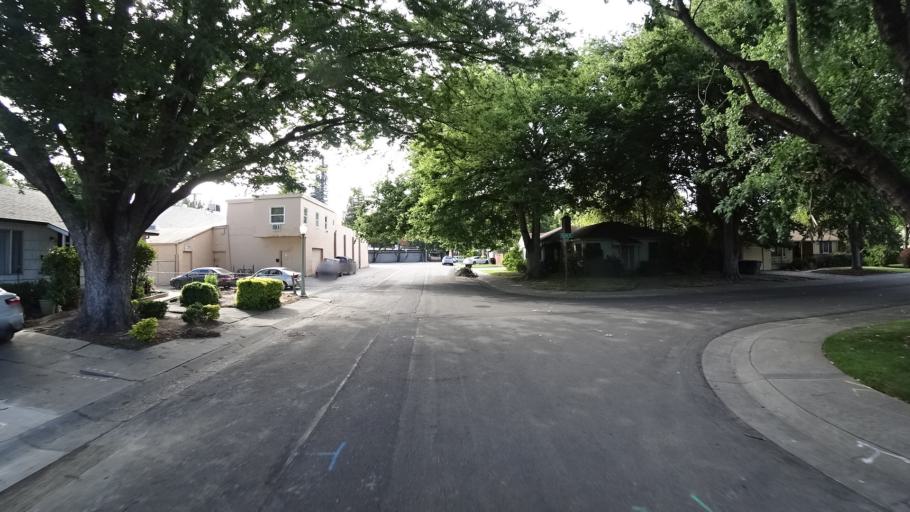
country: US
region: California
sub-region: Sacramento County
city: Sacramento
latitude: 38.5595
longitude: -121.5056
